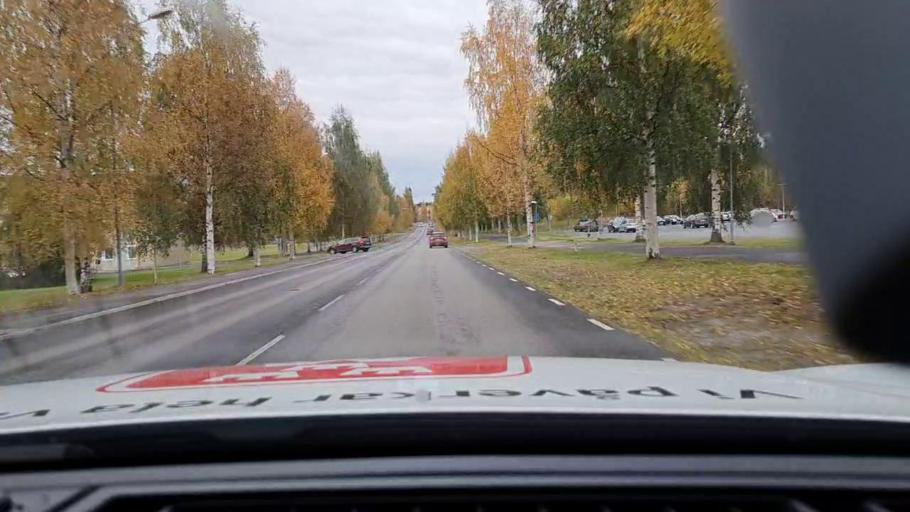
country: SE
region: Norrbotten
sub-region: Bodens Kommun
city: Boden
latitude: 65.8173
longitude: 21.6681
